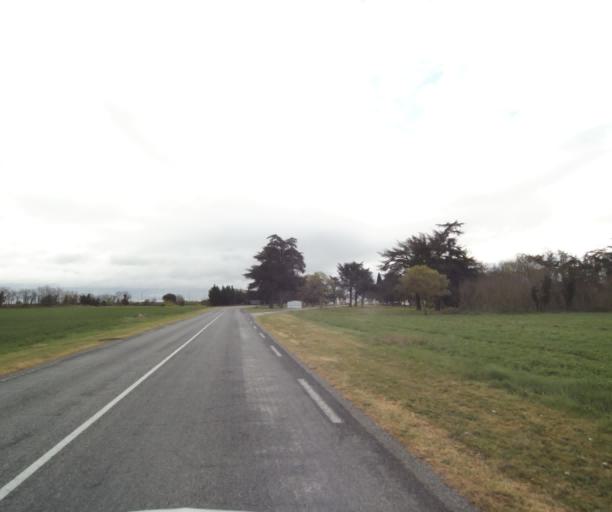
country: FR
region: Midi-Pyrenees
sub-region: Departement de l'Ariege
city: Saverdun
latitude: 43.2309
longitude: 1.5975
